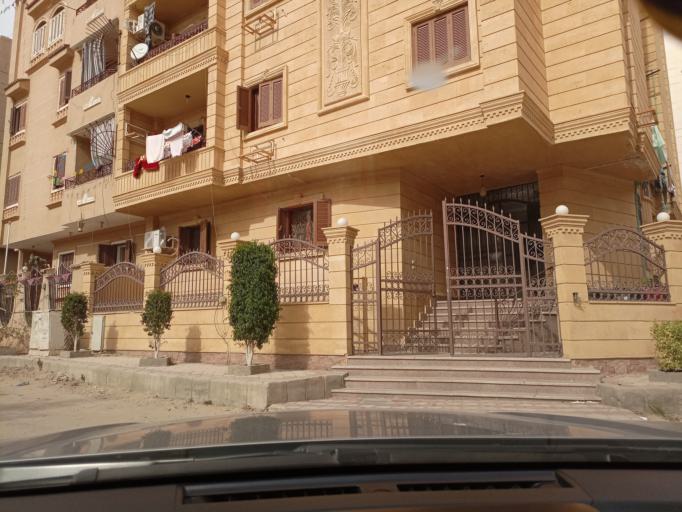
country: EG
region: Muhafazat al Qalyubiyah
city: Al Khankah
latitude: 30.2581
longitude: 31.4785
